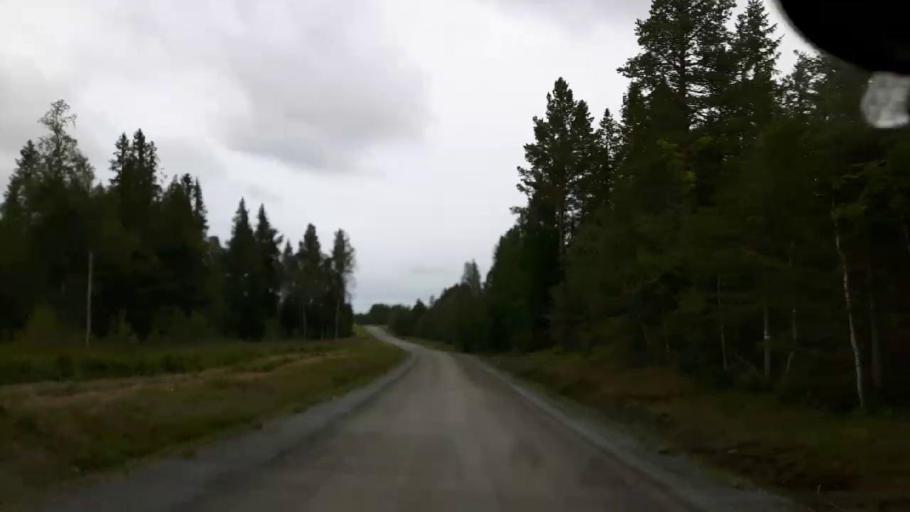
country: SE
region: Jaemtland
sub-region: OEstersunds Kommun
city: Ostersund
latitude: 63.1044
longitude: 14.5465
